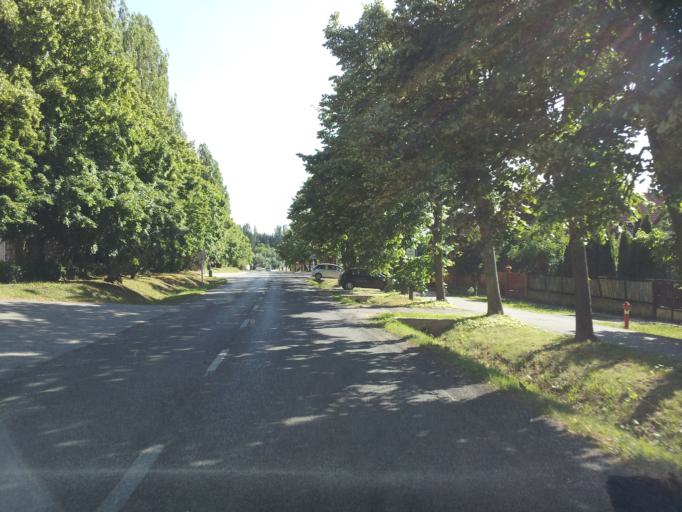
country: HU
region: Veszprem
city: Veszprem
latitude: 47.0861
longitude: 17.8997
